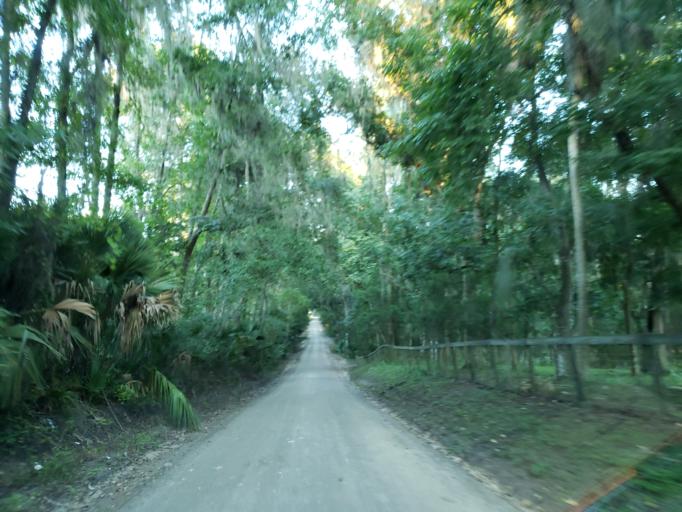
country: US
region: Florida
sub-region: Marion County
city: Citra
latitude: 29.4843
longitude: -82.2533
